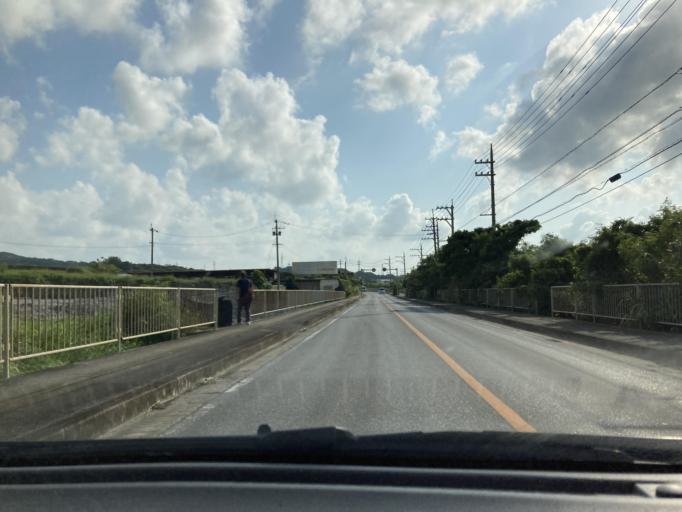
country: JP
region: Okinawa
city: Itoman
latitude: 26.1425
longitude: 127.7021
